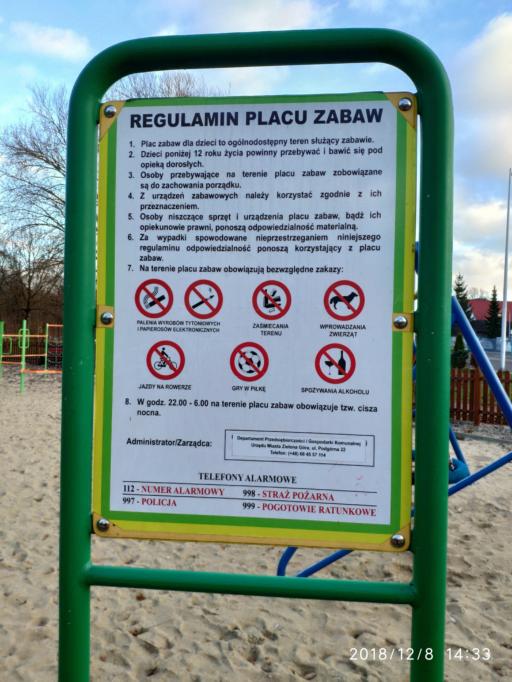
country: PL
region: Lubusz
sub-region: Zielona Gora
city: Zielona Gora
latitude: 51.9500
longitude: 15.5233
